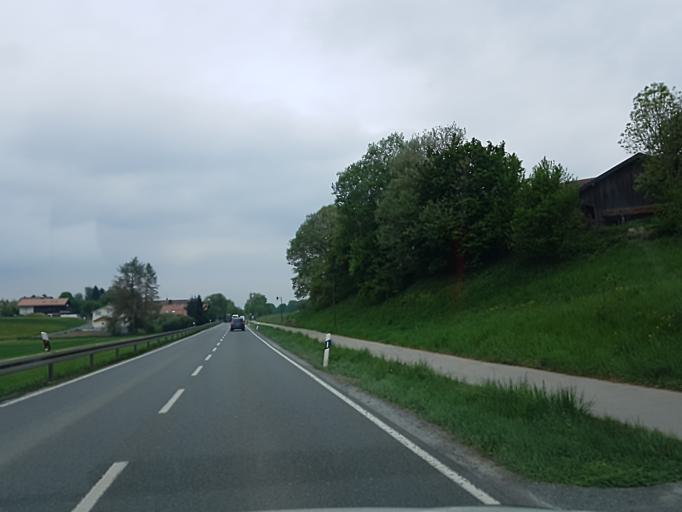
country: DE
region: Bavaria
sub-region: Upper Bavaria
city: Ebersberg
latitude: 48.0911
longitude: 11.9658
